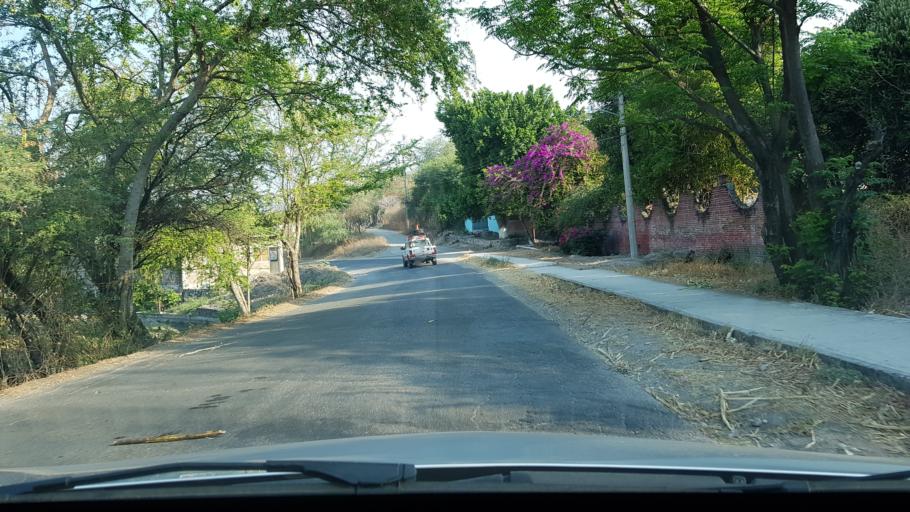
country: MX
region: Morelos
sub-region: Tlaltizapan de Zapata
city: Colonia Palo Prieto (Chipitongo)
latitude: 18.6957
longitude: -99.1019
